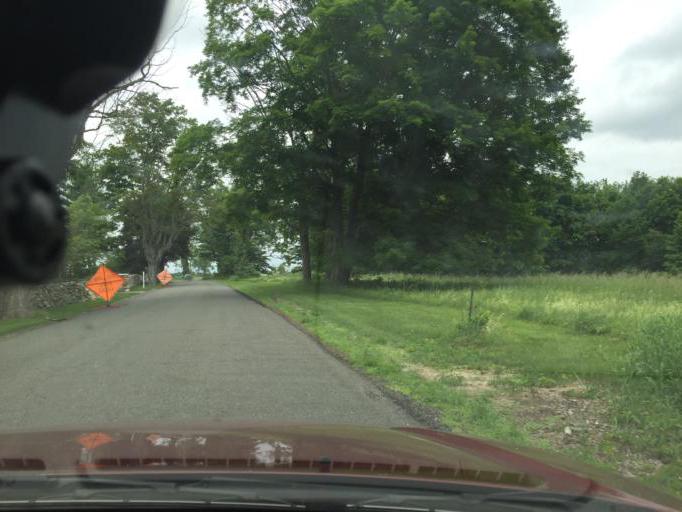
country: US
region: Connecticut
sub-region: Litchfield County
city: Litchfield
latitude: 41.7997
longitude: -73.2560
